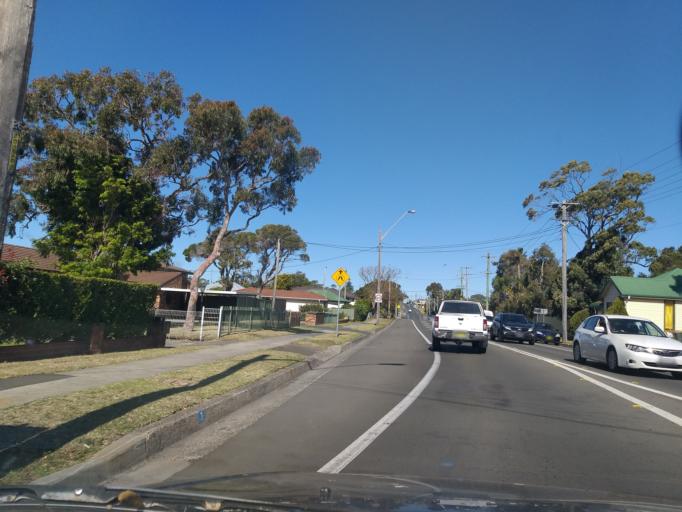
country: AU
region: New South Wales
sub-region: Wollongong
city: East Corrimal
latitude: -34.3629
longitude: 150.9114
